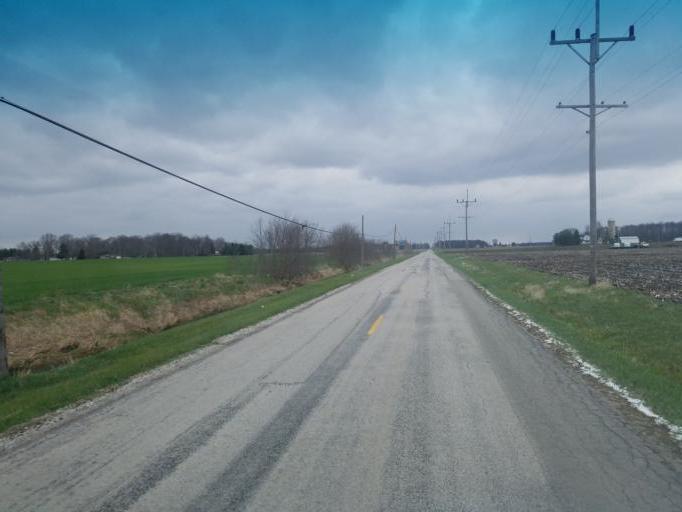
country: US
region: Ohio
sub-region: Marion County
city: Prospect
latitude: 40.4797
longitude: -83.1522
